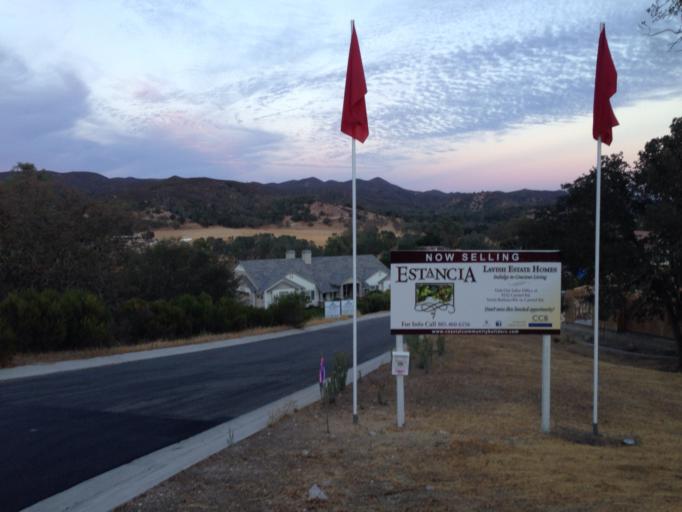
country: US
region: California
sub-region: San Luis Obispo County
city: Atascadero
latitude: 35.4560
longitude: -120.6256
